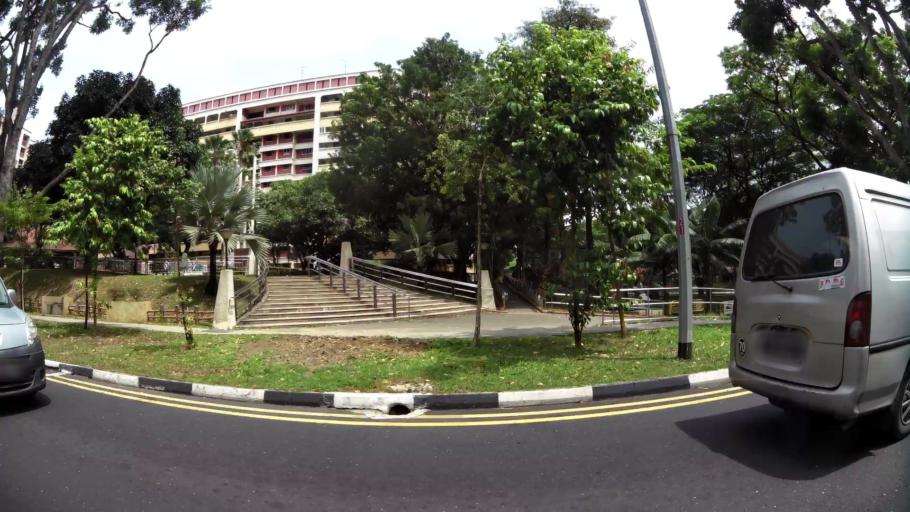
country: SG
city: Singapore
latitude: 1.3478
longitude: 103.7561
